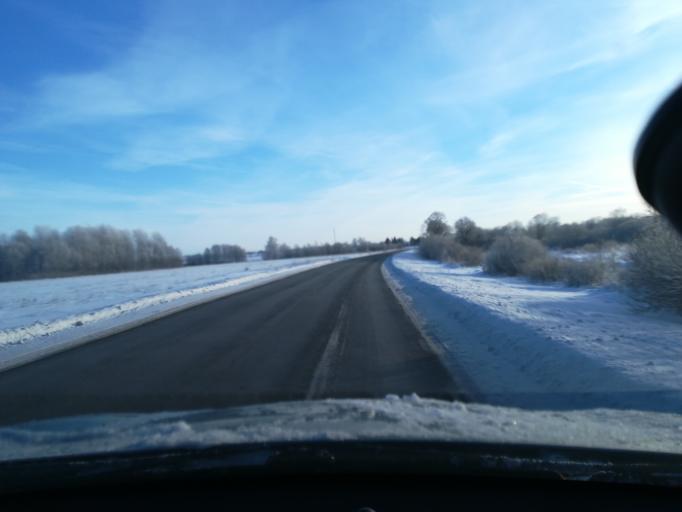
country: EE
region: Harju
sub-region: Harku vald
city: Tabasalu
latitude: 59.3735
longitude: 24.4722
